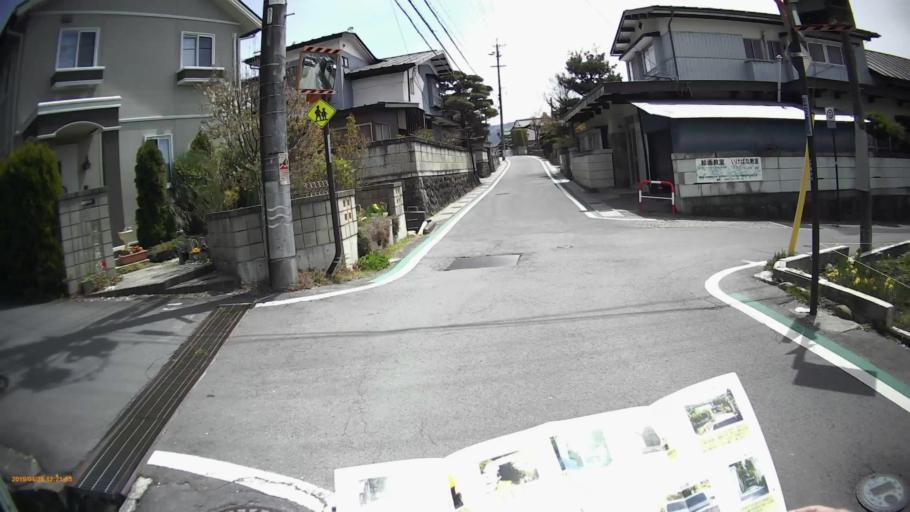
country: JP
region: Nagano
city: Chino
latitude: 36.0147
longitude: 138.1392
